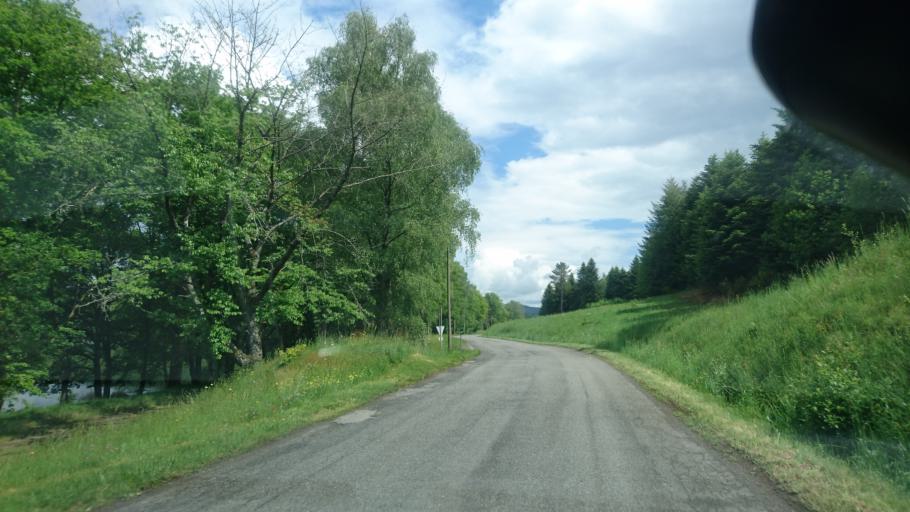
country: FR
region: Limousin
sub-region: Departement de la Haute-Vienne
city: Peyrat-le-Chateau
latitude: 45.7865
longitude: 1.8817
